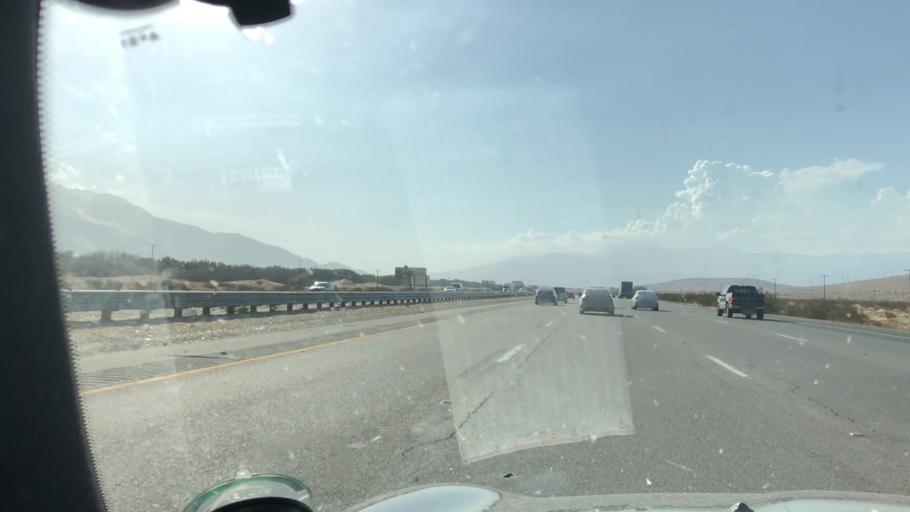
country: US
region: California
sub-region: Riverside County
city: Thousand Palms
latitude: 33.8240
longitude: -116.4152
